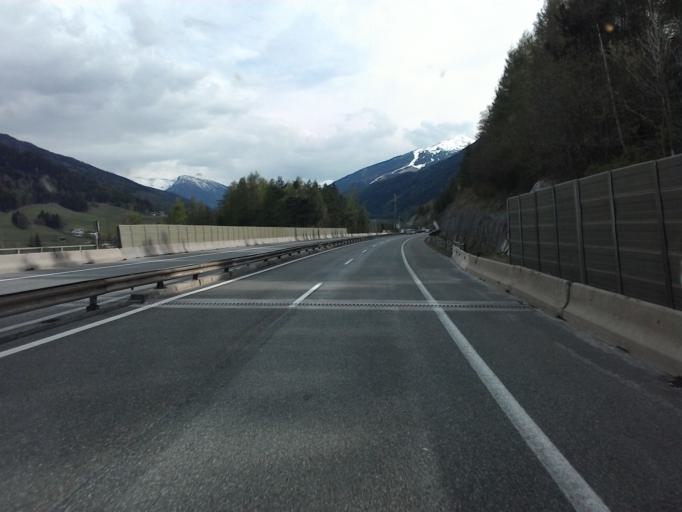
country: AT
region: Tyrol
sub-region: Politischer Bezirk Innsbruck Land
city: Matrei am Brenner
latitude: 47.1347
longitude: 11.4499
